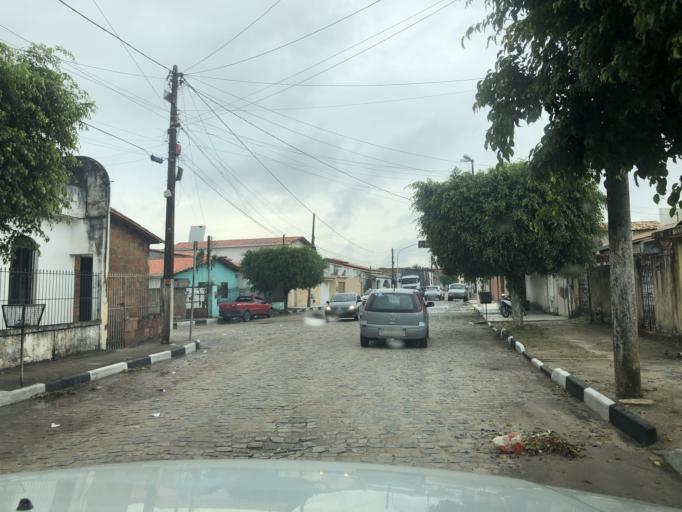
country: BR
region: Bahia
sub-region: Esplanada
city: Esplanada
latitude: -11.7945
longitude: -37.9523
